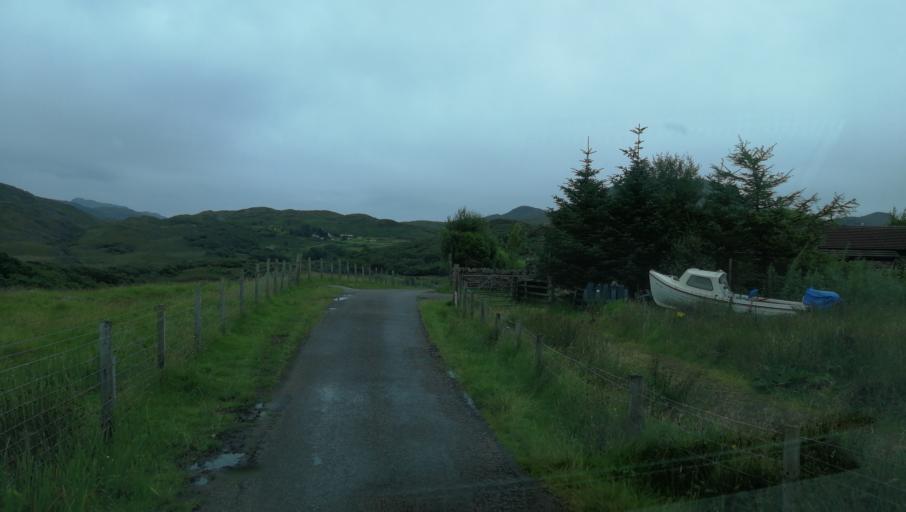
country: GB
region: Scotland
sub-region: Argyll and Bute
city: Isle Of Mull
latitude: 56.7255
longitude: -6.1786
